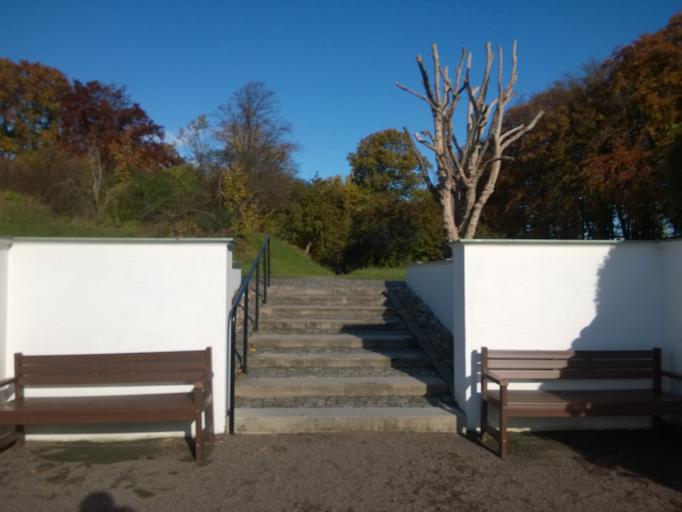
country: SE
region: Skane
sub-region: Burlovs Kommun
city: Arloev
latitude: 55.5960
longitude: 13.0500
